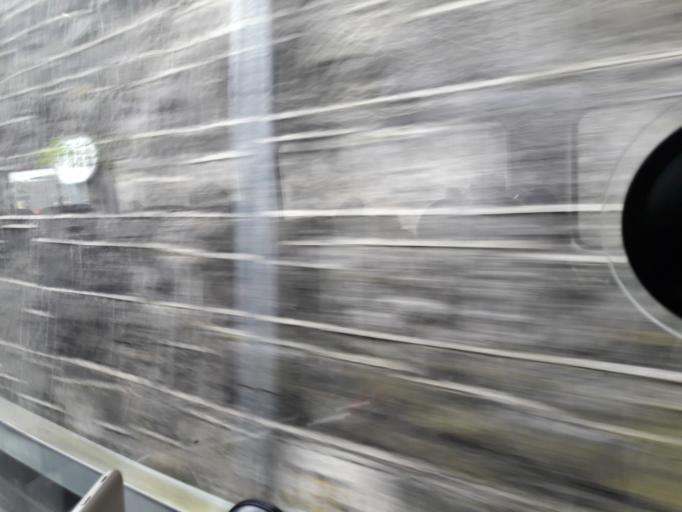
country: IE
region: Leinster
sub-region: An Iarmhi
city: An Muileann gCearr
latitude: 53.5237
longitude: -7.3472
